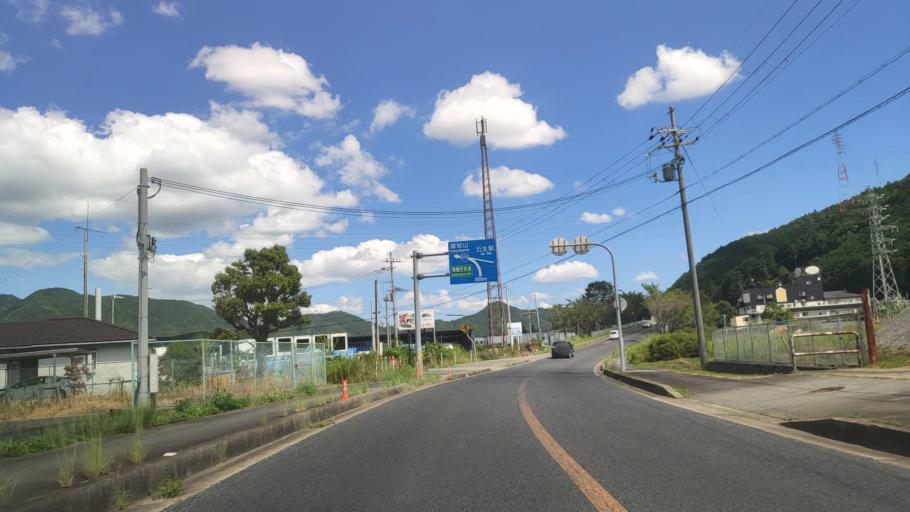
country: JP
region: Kyoto
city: Fukuchiyama
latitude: 35.1620
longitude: 135.0645
